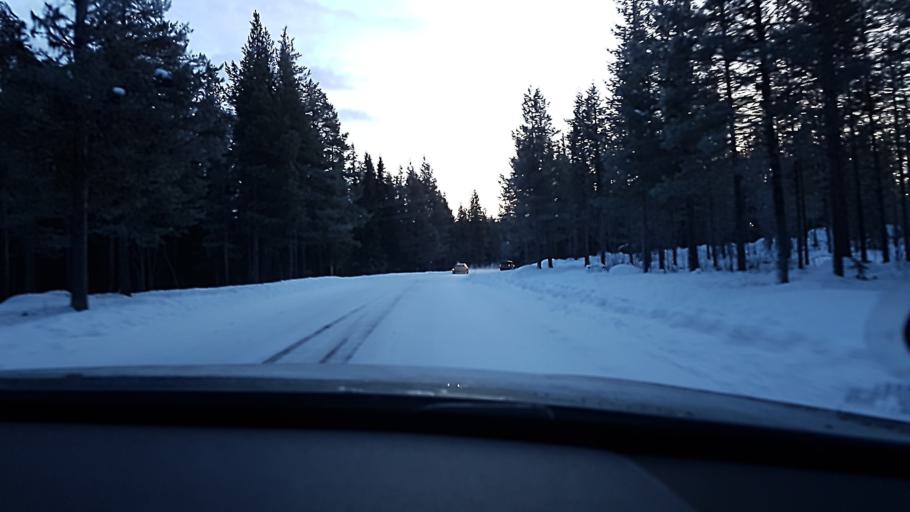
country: SE
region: Vaesterbotten
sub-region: Sorsele Kommun
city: Sorsele
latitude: 65.4982
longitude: 17.5568
